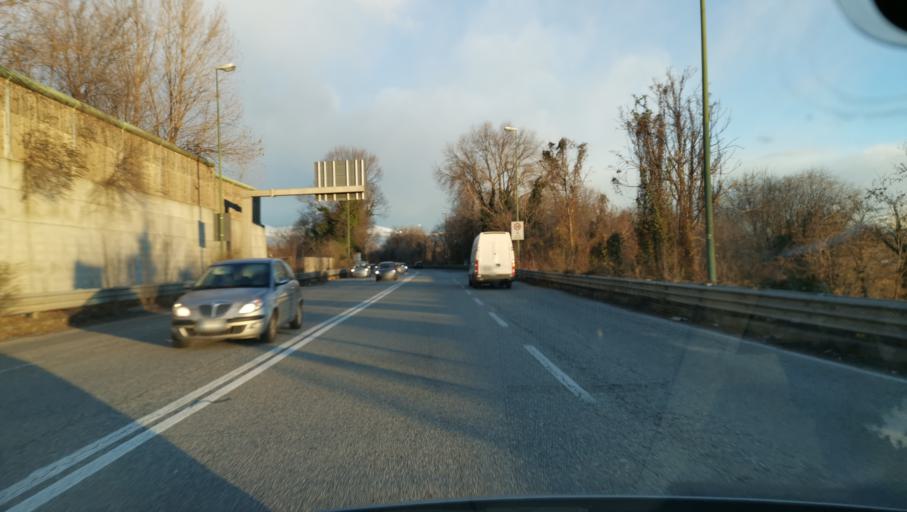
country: IT
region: Piedmont
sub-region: Provincia di Torino
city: Venaria Reale
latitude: 45.1152
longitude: 7.6623
